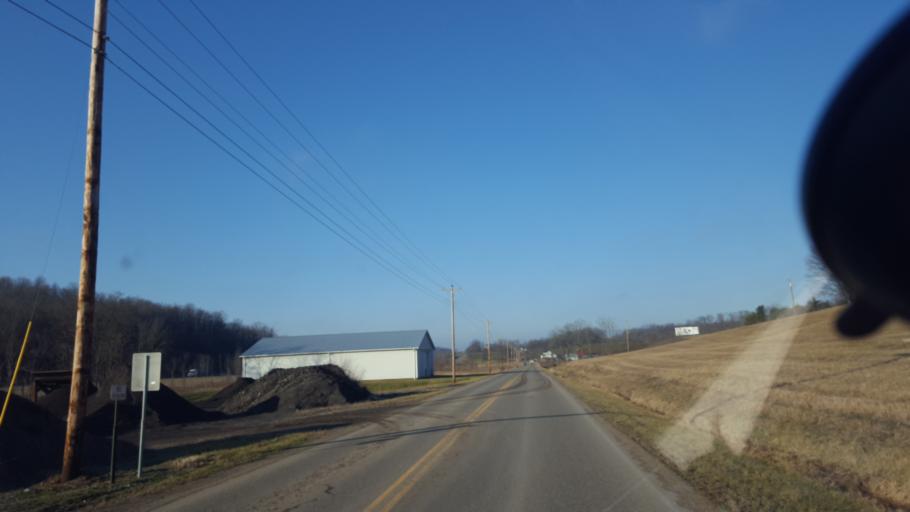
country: US
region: Ohio
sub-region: Belmont County
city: Barnesville
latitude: 40.0505
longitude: -81.3413
